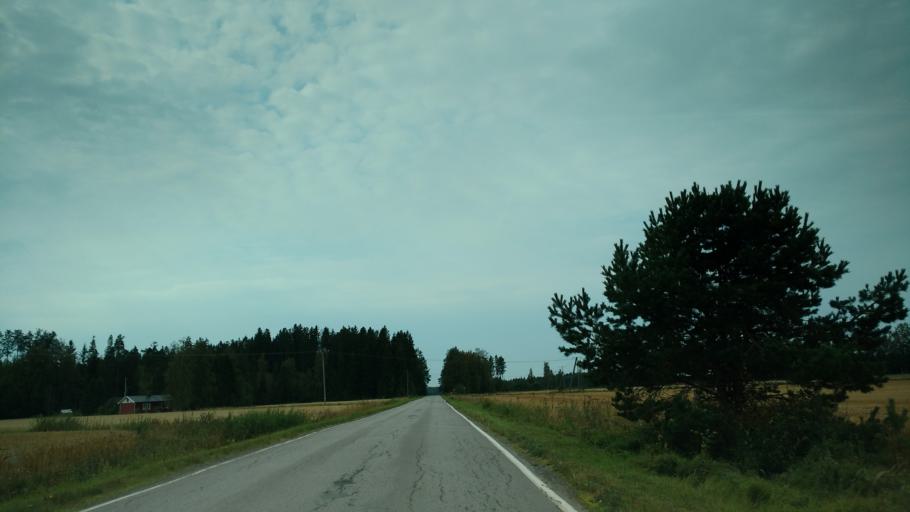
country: FI
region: Varsinais-Suomi
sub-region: Loimaa
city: Koski Tl
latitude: 60.7281
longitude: 23.1845
